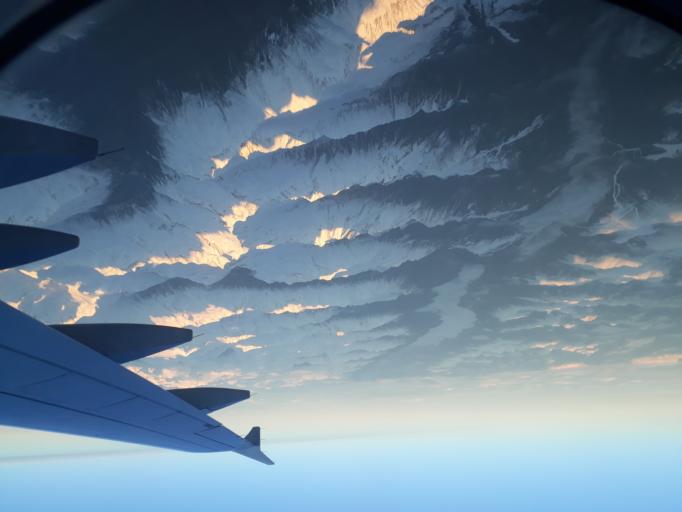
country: AT
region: Tyrol
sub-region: Politischer Bezirk Schwaz
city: Mayrhofen
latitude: 47.1526
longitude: 11.8842
